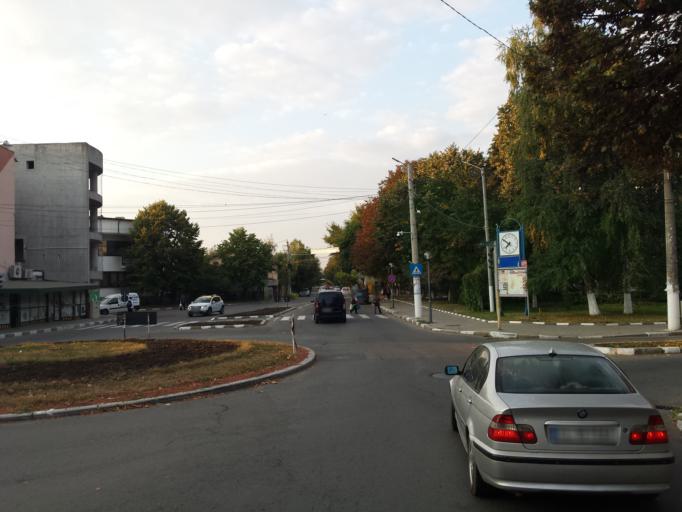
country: RO
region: Calarasi
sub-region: Municipiul Oltenita
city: Oltenita
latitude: 44.0867
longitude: 26.6381
